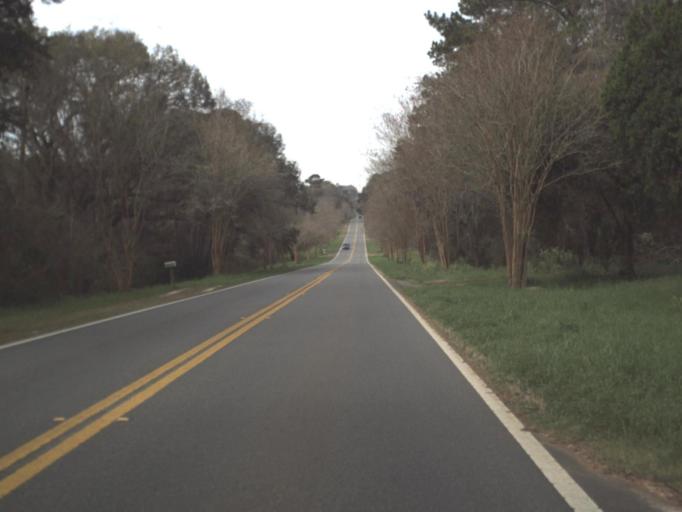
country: US
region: Florida
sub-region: Jefferson County
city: Monticello
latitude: 30.5265
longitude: -84.0071
